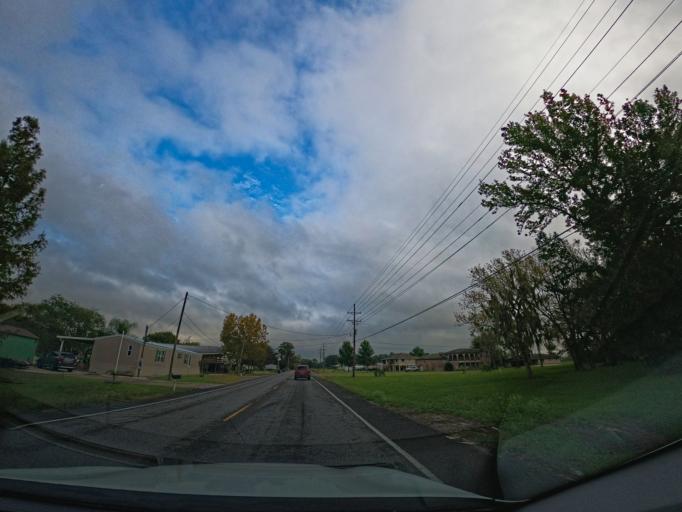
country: US
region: Louisiana
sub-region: Terrebonne Parish
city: Presquille
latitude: 29.4842
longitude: -90.6983
